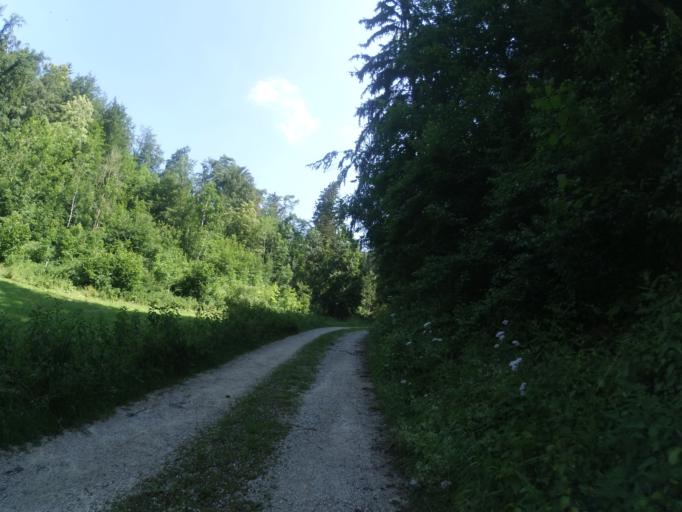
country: DE
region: Baden-Wuerttemberg
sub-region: Tuebingen Region
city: Dornstadt
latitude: 48.4504
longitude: 9.9032
